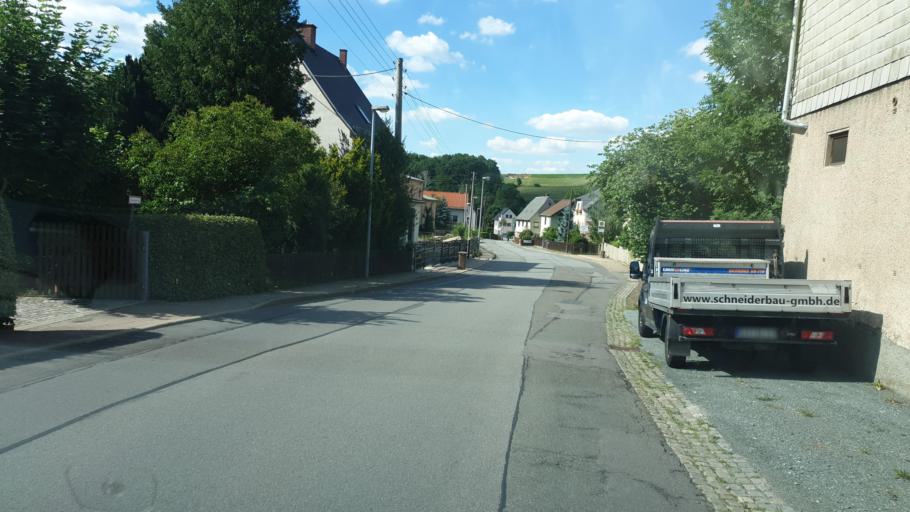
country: DE
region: Saxony
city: Burkhardtsdorf
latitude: 50.7577
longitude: 12.9164
